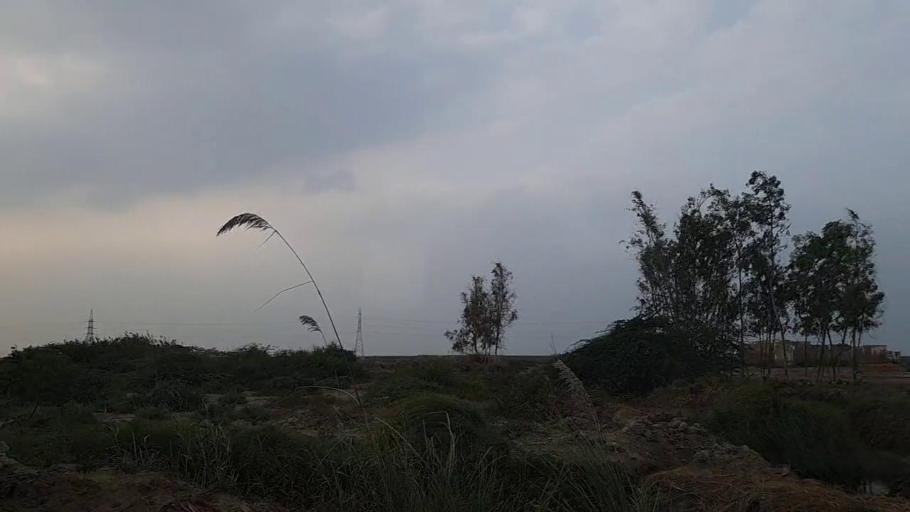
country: PK
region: Sindh
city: Gharo
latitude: 24.6286
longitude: 67.5024
